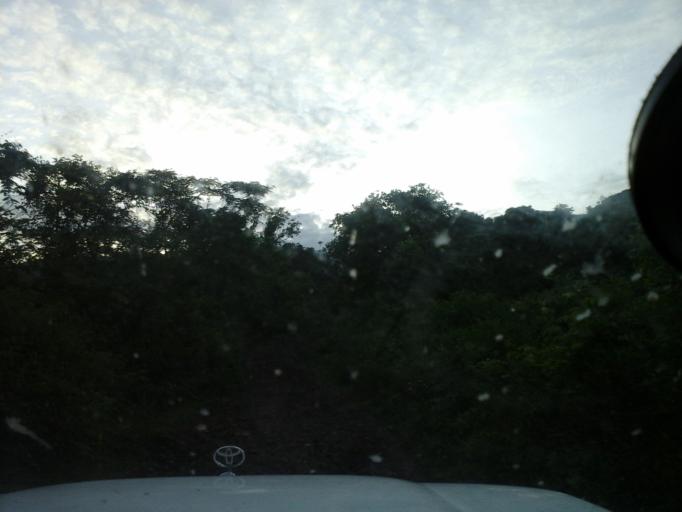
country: CO
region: Cesar
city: Agustin Codazzi
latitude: 10.1733
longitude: -73.1534
